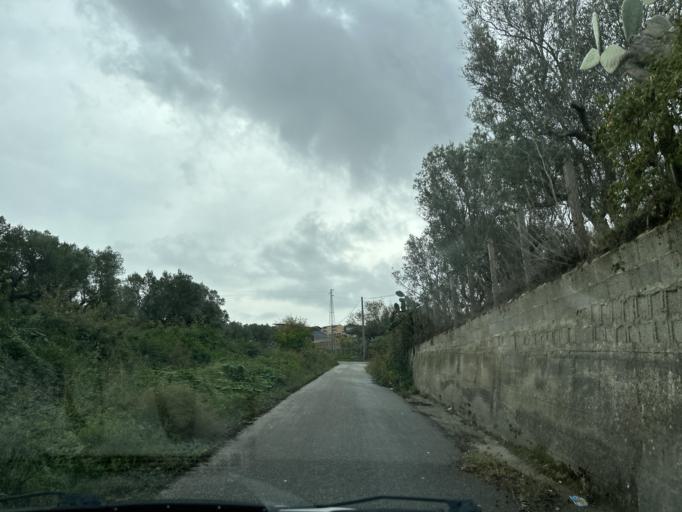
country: IT
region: Calabria
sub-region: Provincia di Catanzaro
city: Staletti
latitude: 38.7691
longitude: 16.5311
